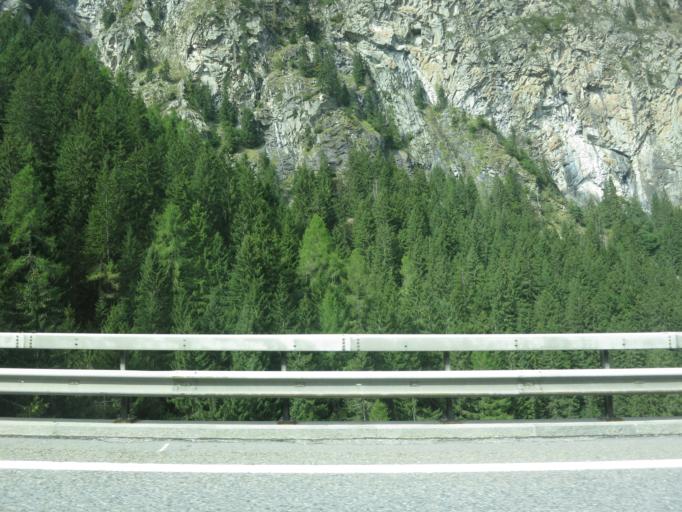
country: CH
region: Grisons
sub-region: Hinterrhein District
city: Thusis
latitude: 46.5761
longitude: 9.4171
